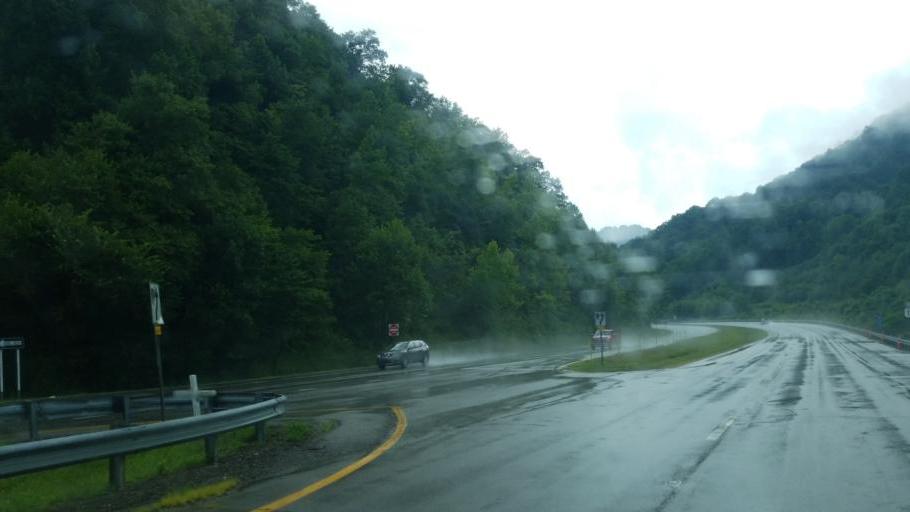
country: US
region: West Virginia
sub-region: Logan County
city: Chapmanville
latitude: 37.9815
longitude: -81.9923
